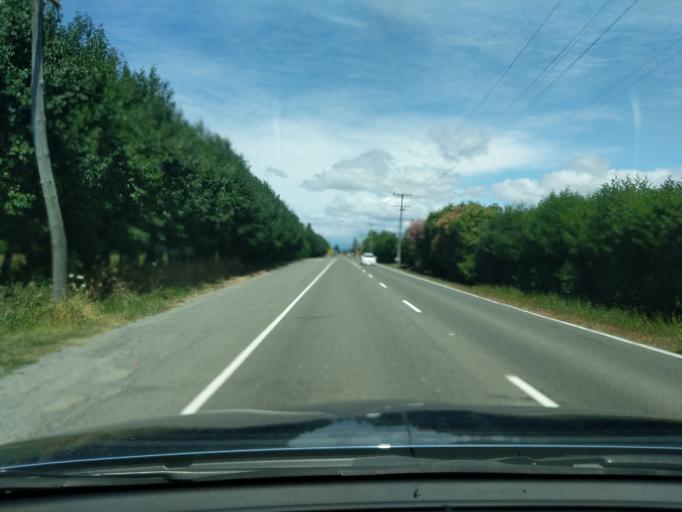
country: NZ
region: Tasman
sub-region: Tasman District
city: Motueka
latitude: -41.0877
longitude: 172.9968
